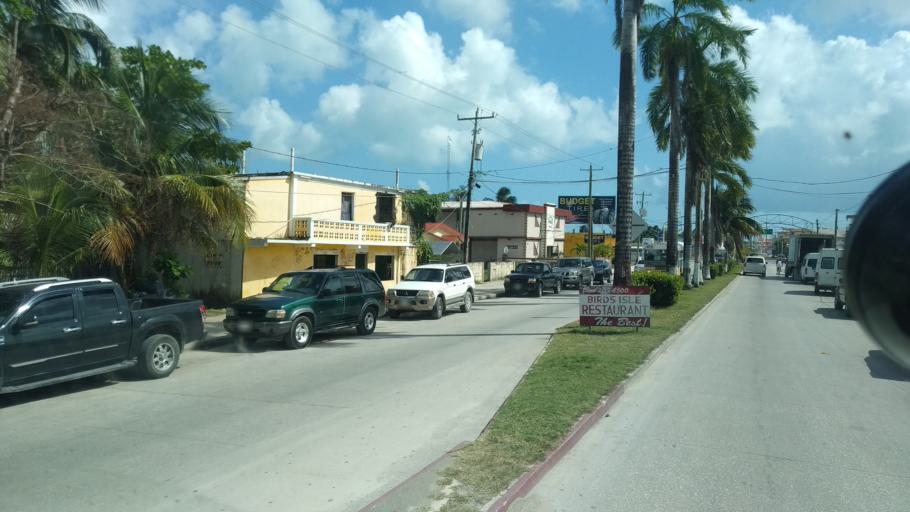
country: BZ
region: Belize
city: Belize City
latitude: 17.4977
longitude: -88.1990
